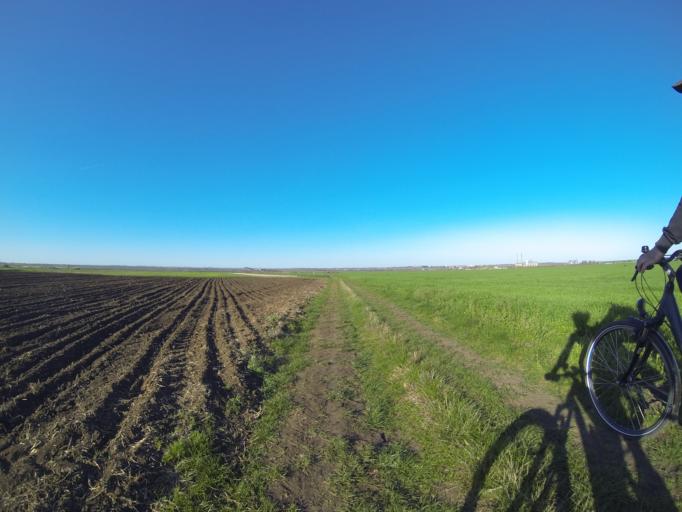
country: RO
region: Dolj
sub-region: Comuna Ceratu
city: Ceratu
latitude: 44.0800
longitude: 23.7058
